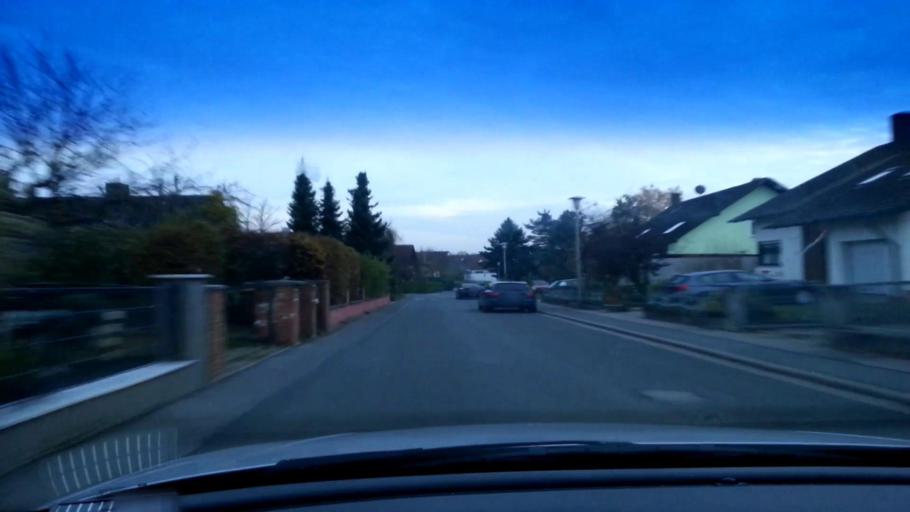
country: DE
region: Bavaria
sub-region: Upper Franconia
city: Breitengussbach
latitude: 49.9757
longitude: 10.8966
